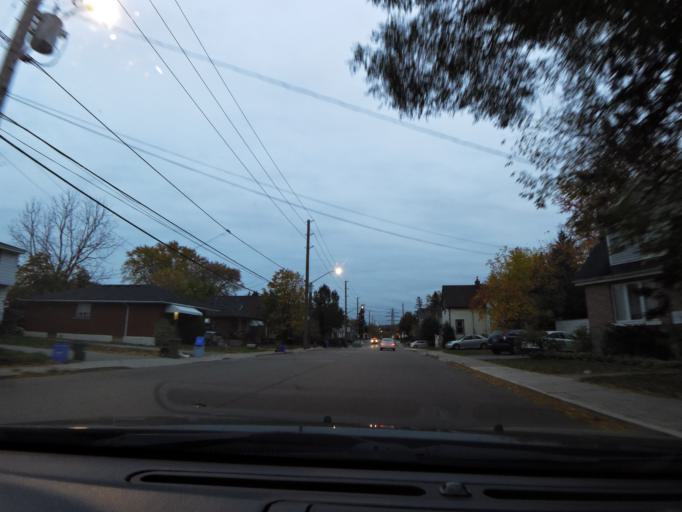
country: CA
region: Ontario
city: Ancaster
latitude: 43.2533
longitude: -79.9262
